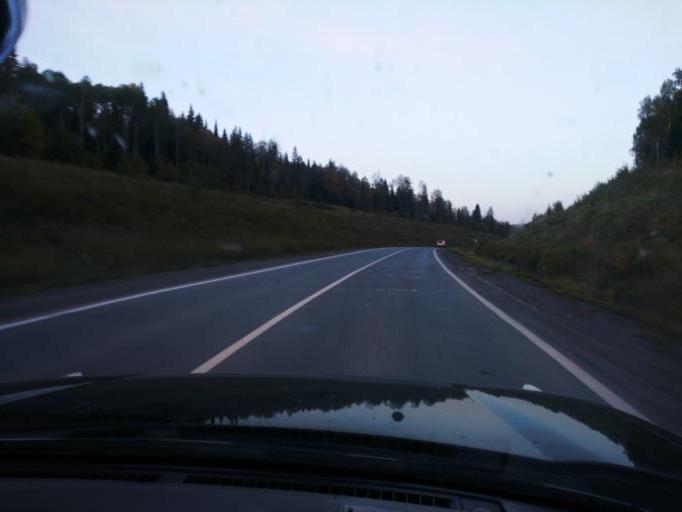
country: RU
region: Perm
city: Sylva
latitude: 58.3026
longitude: 56.7822
